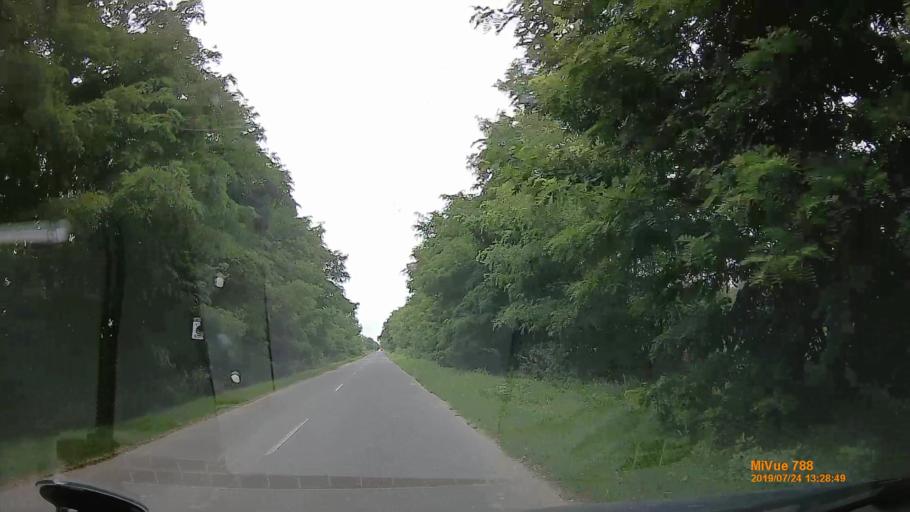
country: UA
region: Zakarpattia
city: Batiovo
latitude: 48.2241
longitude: 22.4107
